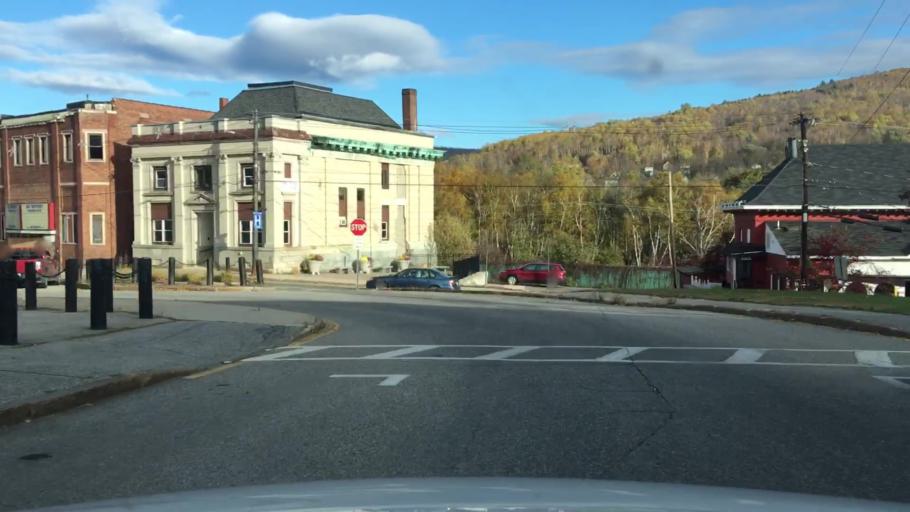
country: US
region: New Hampshire
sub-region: Coos County
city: Berlin
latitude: 44.4677
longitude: -71.1840
